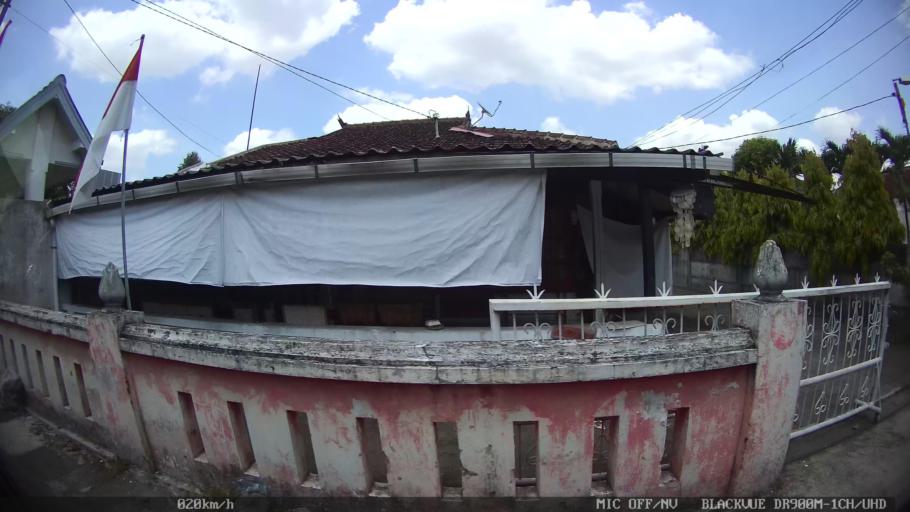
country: ID
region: Daerah Istimewa Yogyakarta
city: Gamping Lor
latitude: -7.8042
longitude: 110.3476
